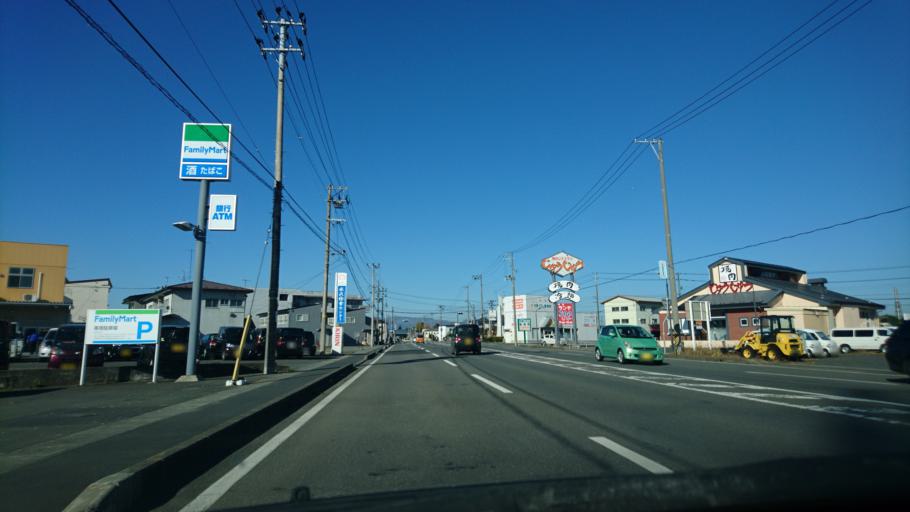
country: JP
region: Iwate
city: Mizusawa
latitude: 39.1426
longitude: 141.1254
